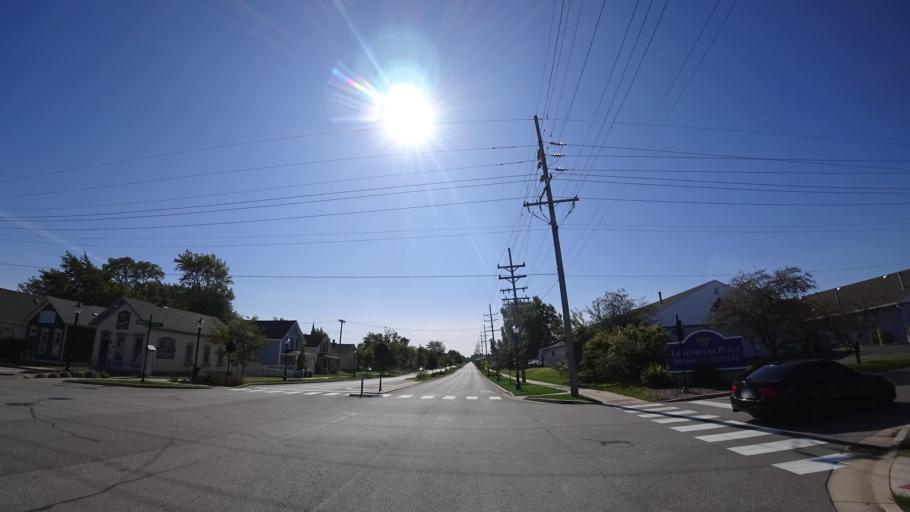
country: US
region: Indiana
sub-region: LaPorte County
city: Michigan City
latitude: 41.7176
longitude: -86.9055
